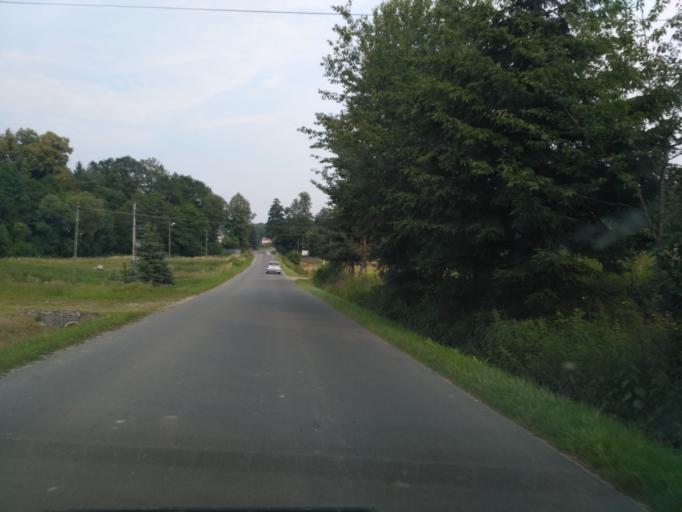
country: PL
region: Subcarpathian Voivodeship
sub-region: Powiat strzyzowski
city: Konieczkowa
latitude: 49.8395
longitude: 21.9405
